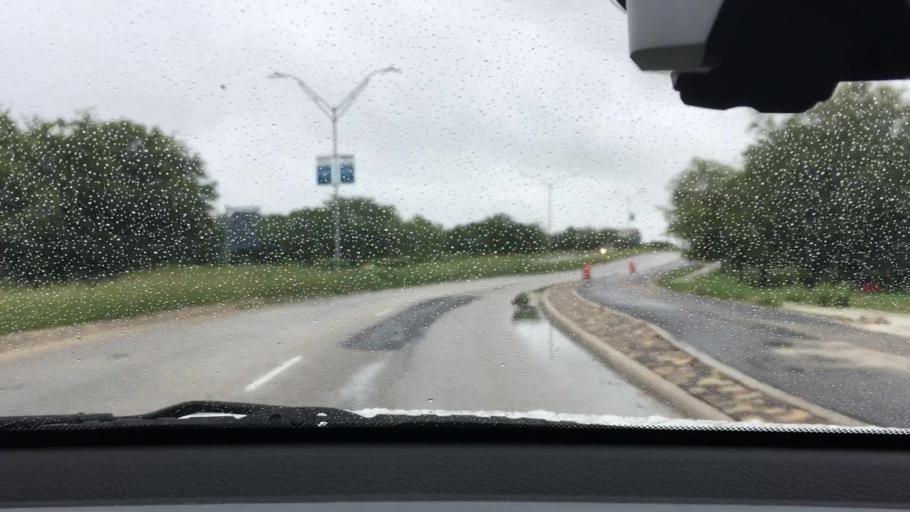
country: US
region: Texas
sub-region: Bexar County
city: Leon Valley
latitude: 29.5217
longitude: -98.5907
